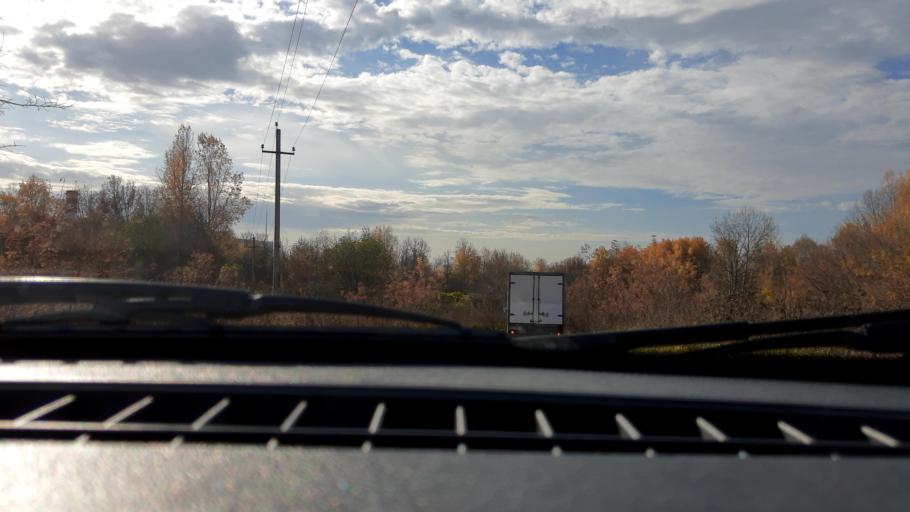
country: RU
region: Bashkortostan
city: Mikhaylovka
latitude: 54.8067
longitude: 55.8357
